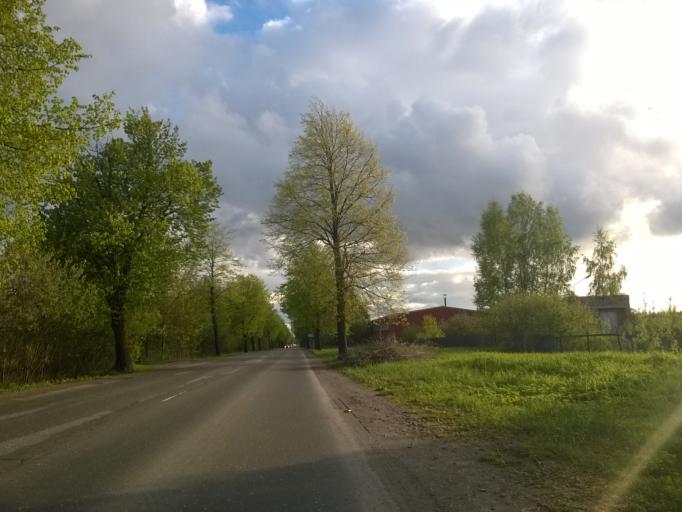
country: LV
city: Tireli
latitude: 56.9370
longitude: 23.5970
